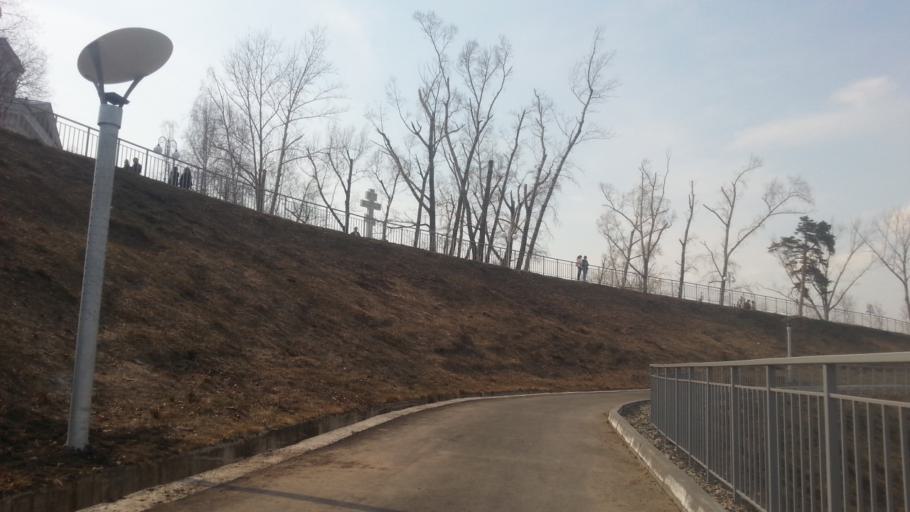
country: RU
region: Altai Krai
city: Zaton
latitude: 53.3240
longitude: 83.7966
